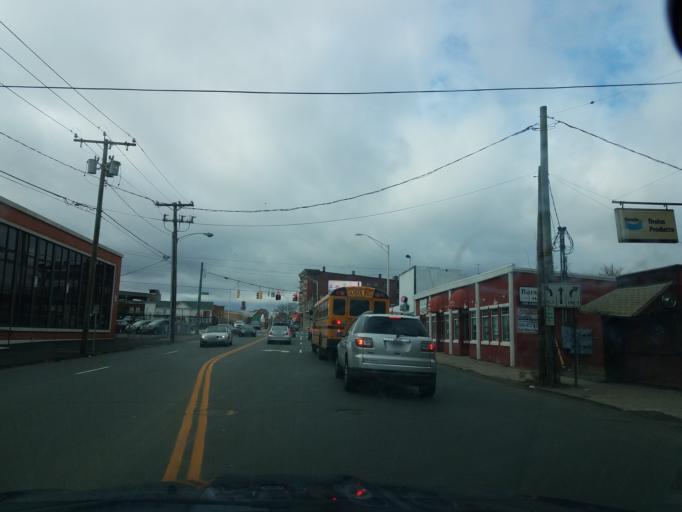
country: US
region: Connecticut
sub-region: New Haven County
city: Waterbury
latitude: 41.5544
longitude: -73.0334
